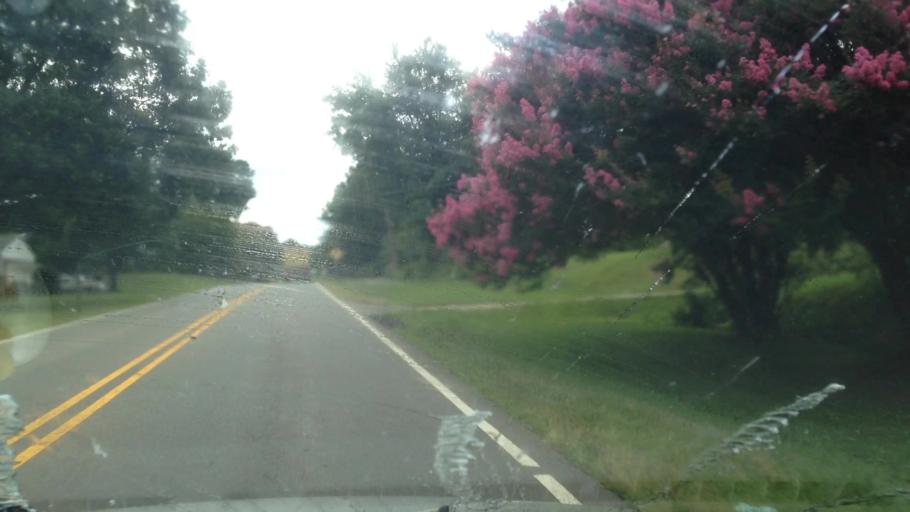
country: US
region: North Carolina
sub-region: Rockingham County
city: Wentworth
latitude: 36.3998
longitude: -79.7739
